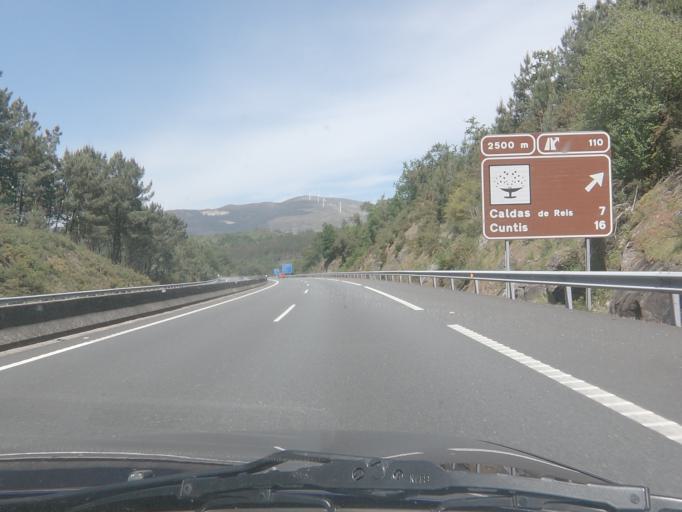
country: ES
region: Galicia
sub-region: Provincia de Pontevedra
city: Portas
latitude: 42.5789
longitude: -8.6734
